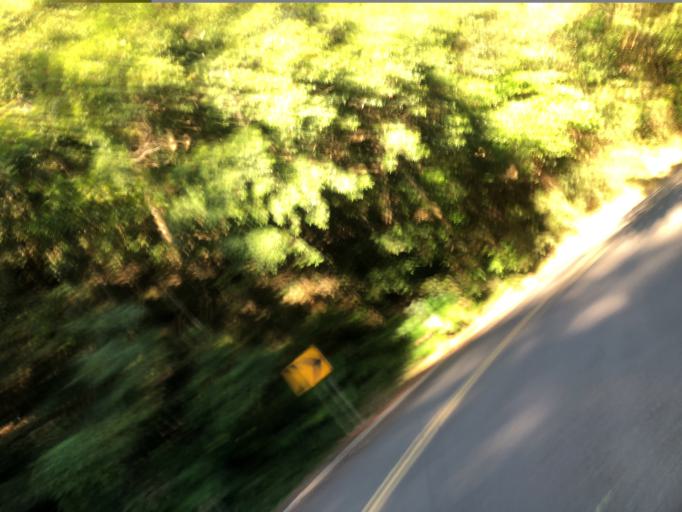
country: TW
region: Taiwan
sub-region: Miaoli
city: Miaoli
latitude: 24.5815
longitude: 120.9307
